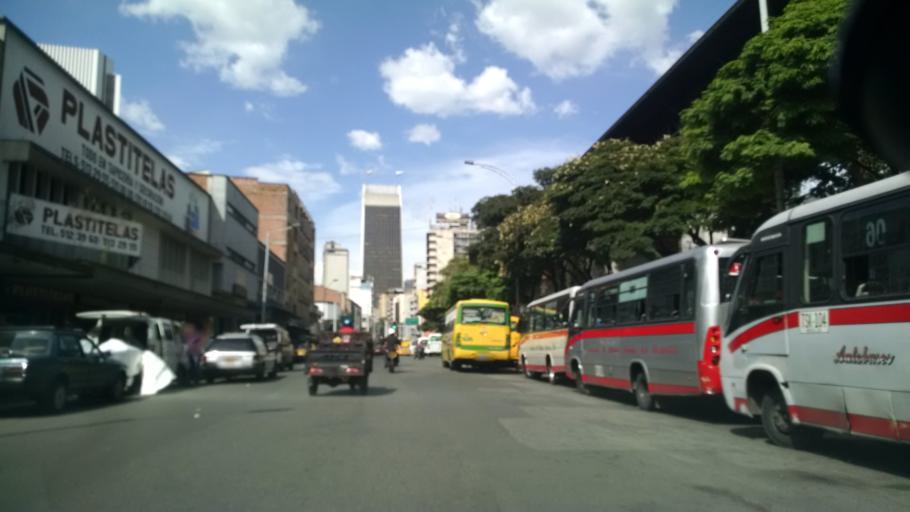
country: CO
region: Antioquia
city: Medellin
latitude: 6.2457
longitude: -75.5690
